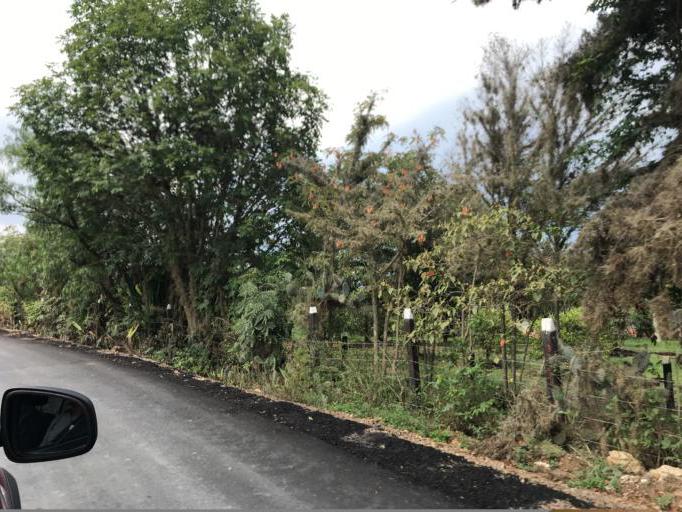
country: CO
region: Boyaca
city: Villa de Leiva
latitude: 5.6425
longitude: -73.5972
